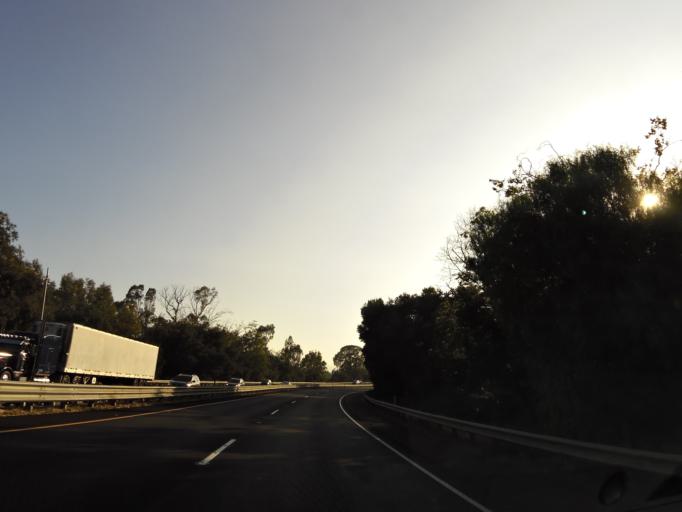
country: US
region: California
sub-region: San Luis Obispo County
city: San Luis Obispo
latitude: 35.2926
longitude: -120.6442
